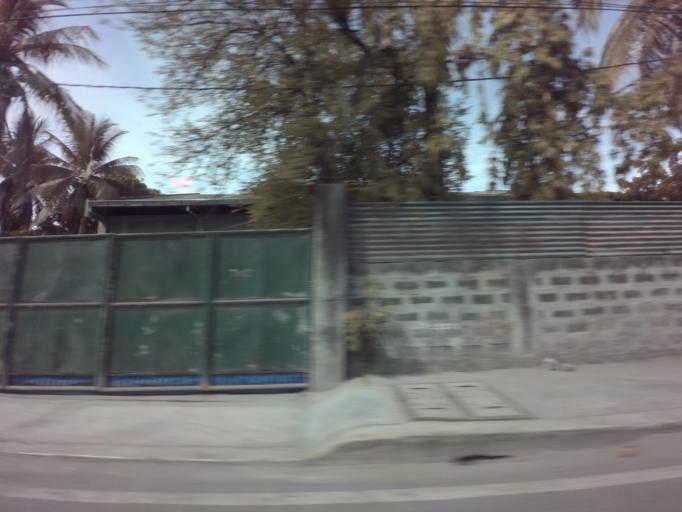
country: PH
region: Calabarzon
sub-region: Province of Rizal
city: Pateros
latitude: 14.5405
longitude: 121.0891
